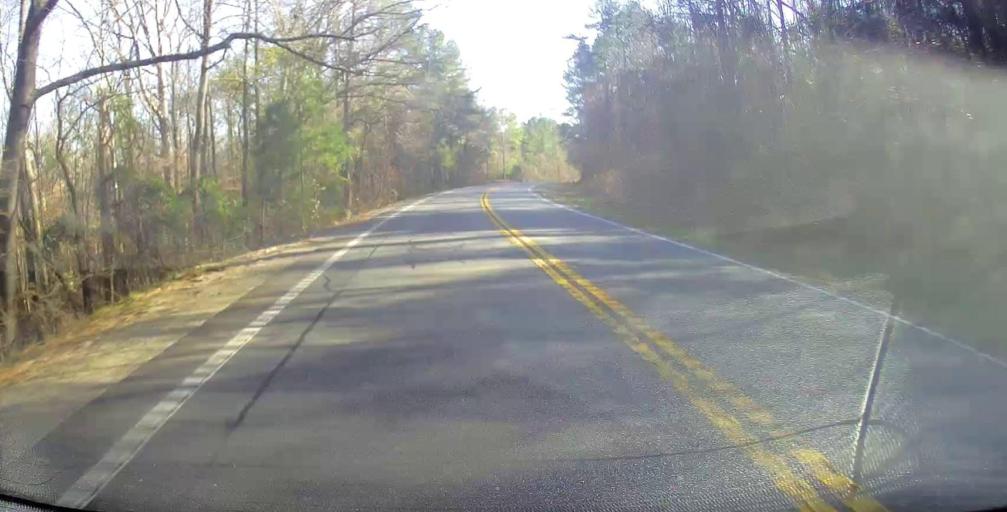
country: US
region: Georgia
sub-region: Talbot County
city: Talbotton
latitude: 32.7496
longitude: -84.5543
